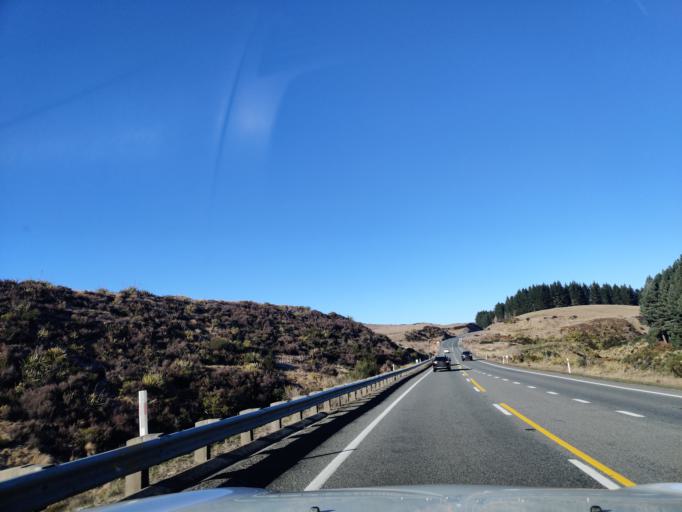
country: NZ
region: Manawatu-Wanganui
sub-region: Ruapehu District
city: Waiouru
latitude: -39.4431
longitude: 175.6813
